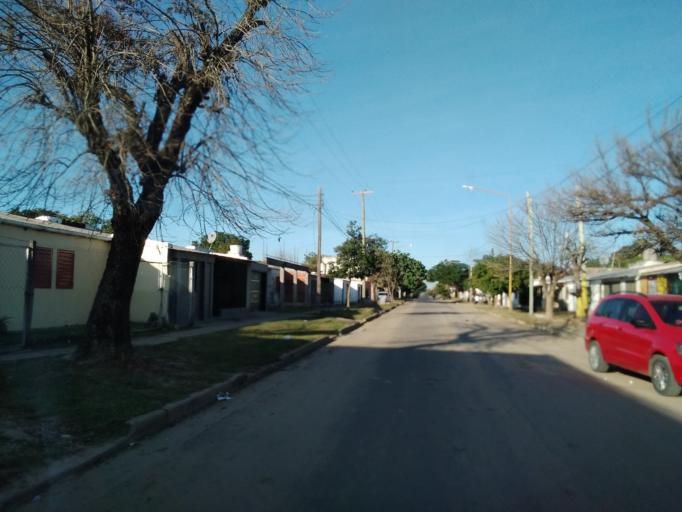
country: AR
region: Corrientes
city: Corrientes
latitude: -27.5026
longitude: -58.8357
